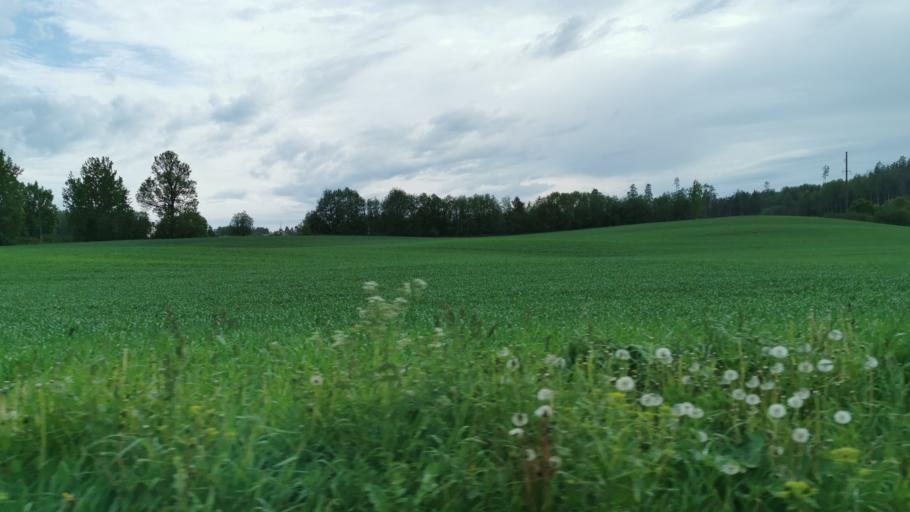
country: EE
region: Laeaene-Virumaa
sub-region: Rakvere linn
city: Rakvere
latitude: 59.2687
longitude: 26.3577
